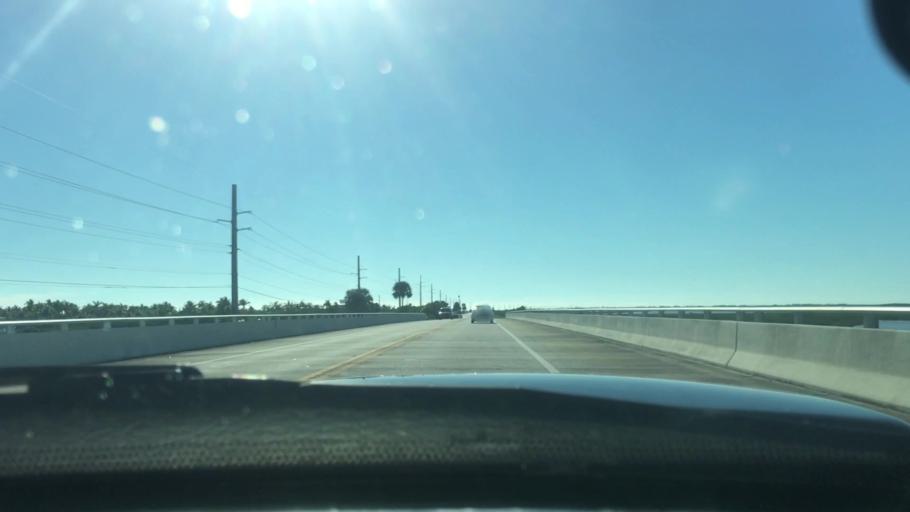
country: US
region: Florida
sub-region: Monroe County
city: Big Coppitt Key
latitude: 24.6268
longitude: -81.5972
